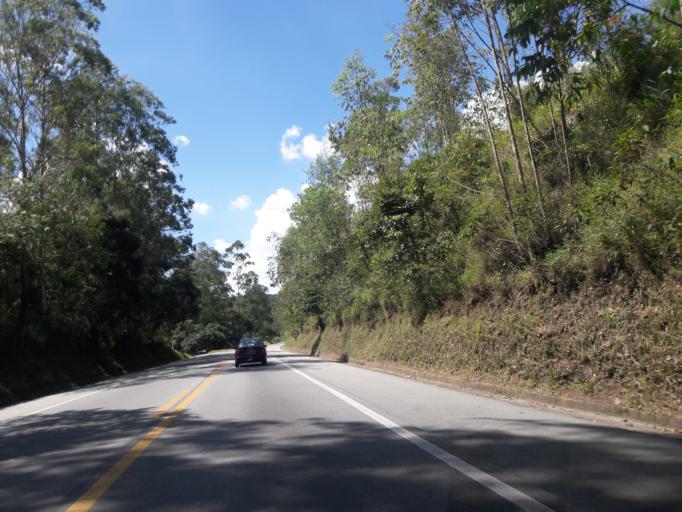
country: BR
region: Sao Paulo
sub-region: Francisco Morato
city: Francisco Morato
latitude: -23.2797
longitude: -46.7953
